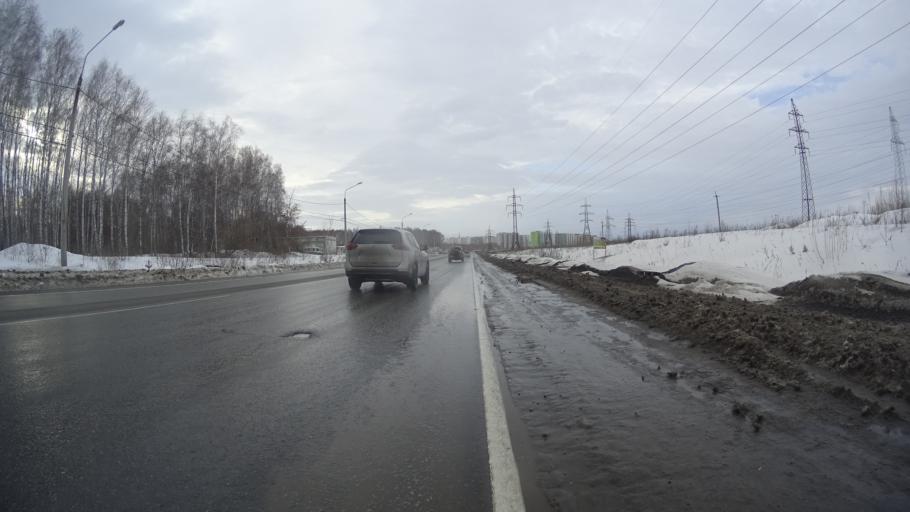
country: RU
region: Chelyabinsk
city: Roshchino
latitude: 55.2095
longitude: 61.3159
